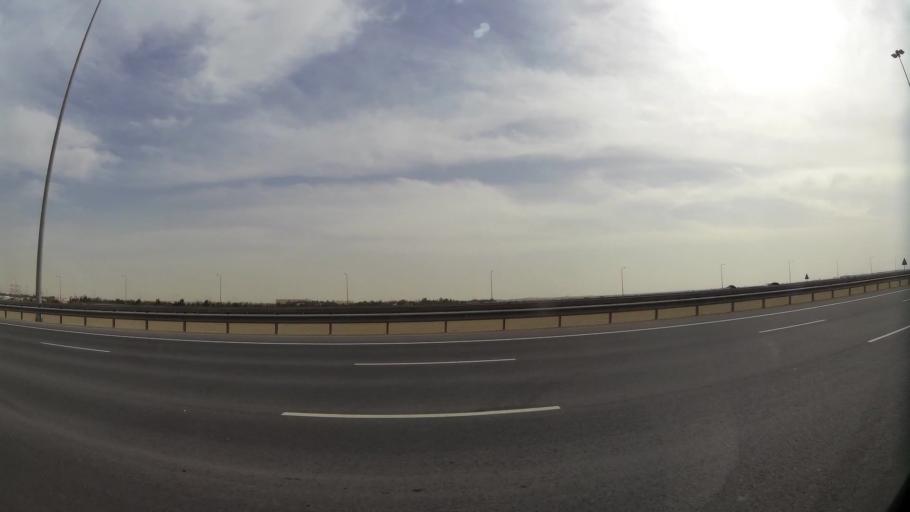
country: QA
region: Baladiyat ar Rayyan
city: Ash Shahaniyah
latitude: 25.3514
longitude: 51.2959
